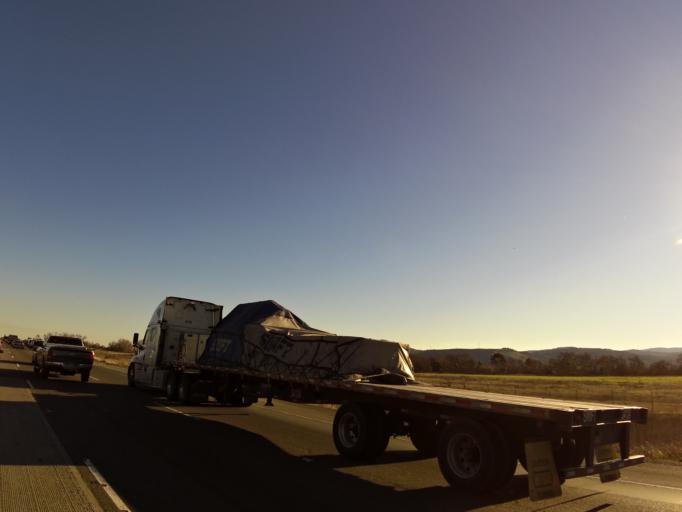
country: US
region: California
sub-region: Santa Clara County
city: Morgan Hill
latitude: 37.1748
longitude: -121.6756
